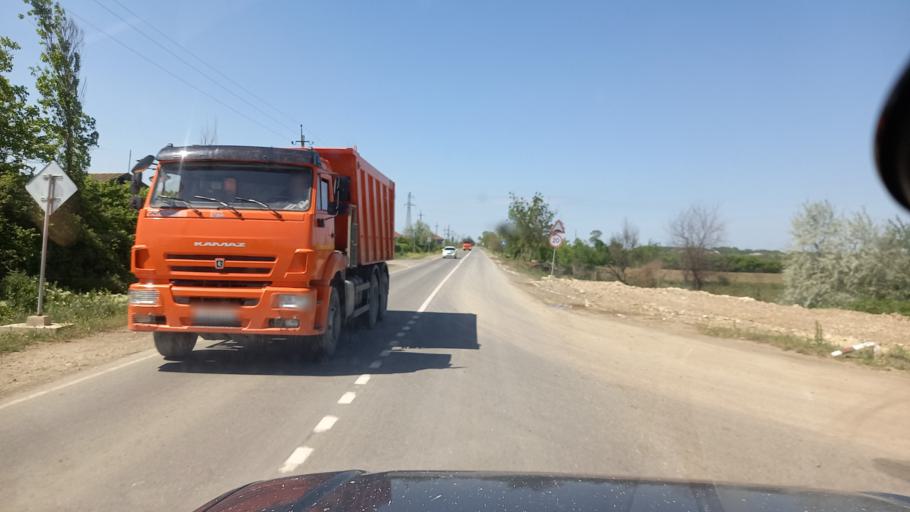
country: RU
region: Dagestan
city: Novaya Maka
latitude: 41.8201
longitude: 48.4013
